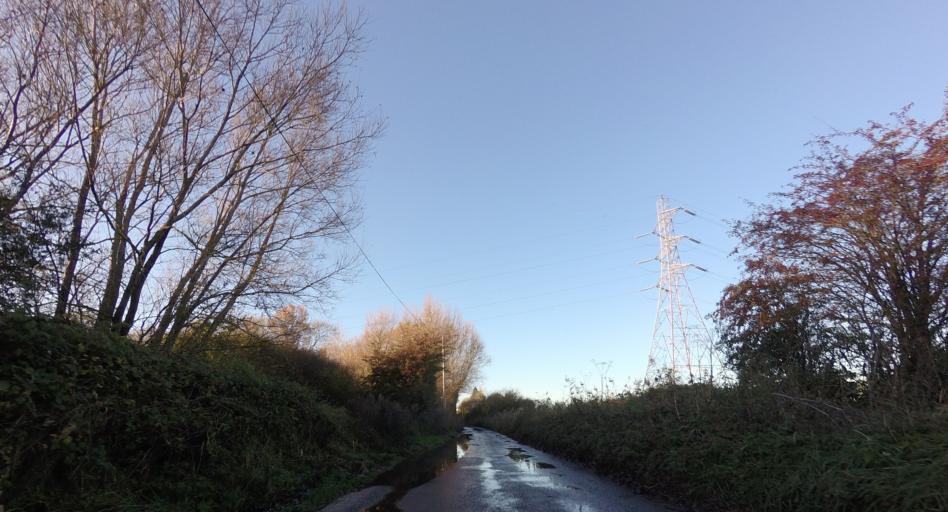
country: GB
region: England
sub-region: West Sussex
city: Steyning
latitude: 50.8940
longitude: -0.3133
